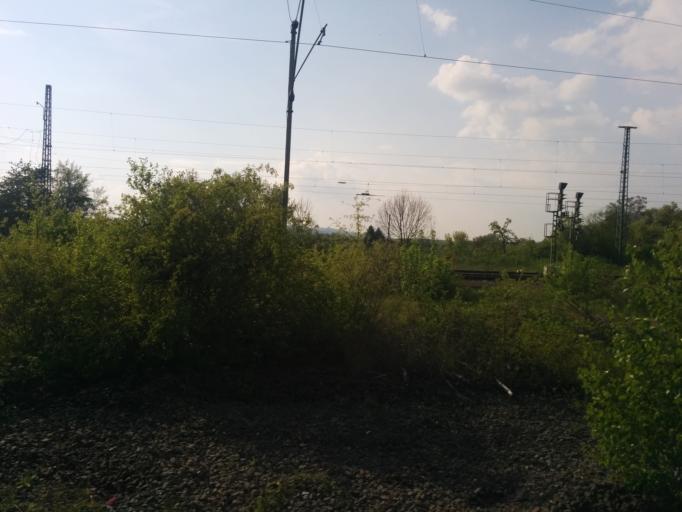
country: DE
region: Lower Saxony
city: Northeim
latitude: 51.7013
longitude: 9.9856
